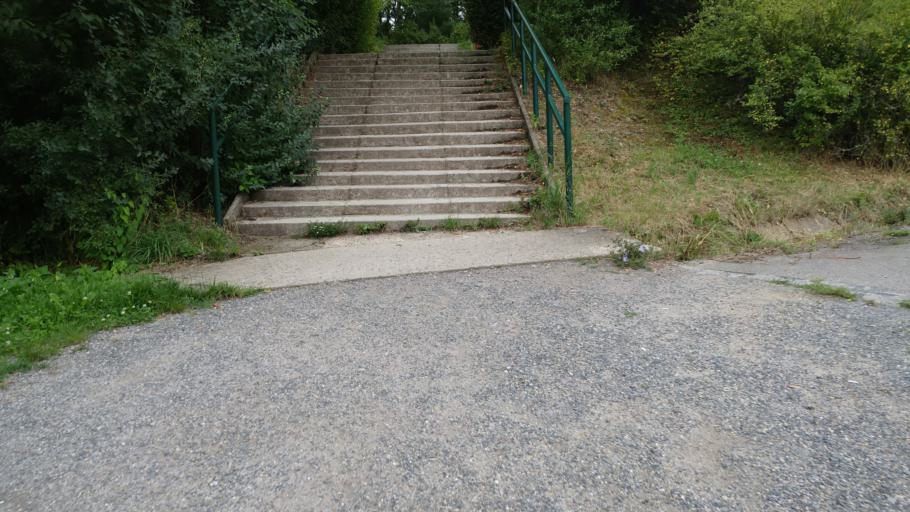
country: CZ
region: Central Bohemia
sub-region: Okres Praha-Zapad
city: Pruhonice
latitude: 50.0395
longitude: 14.5328
